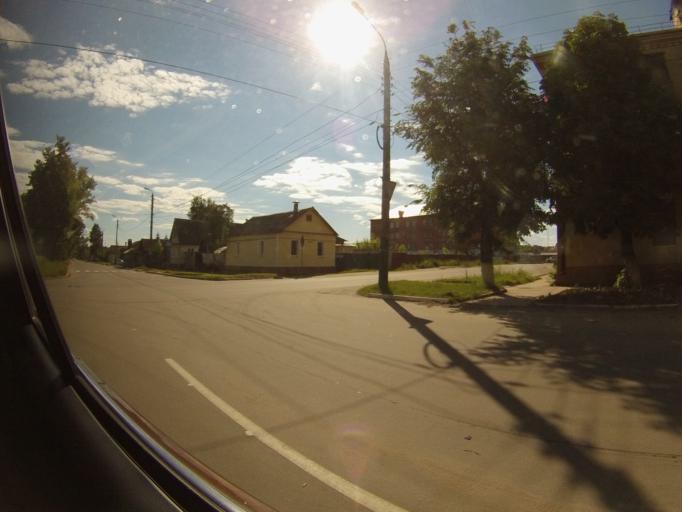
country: RU
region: Orjol
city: Mtsensk
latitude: 53.2762
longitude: 36.5721
